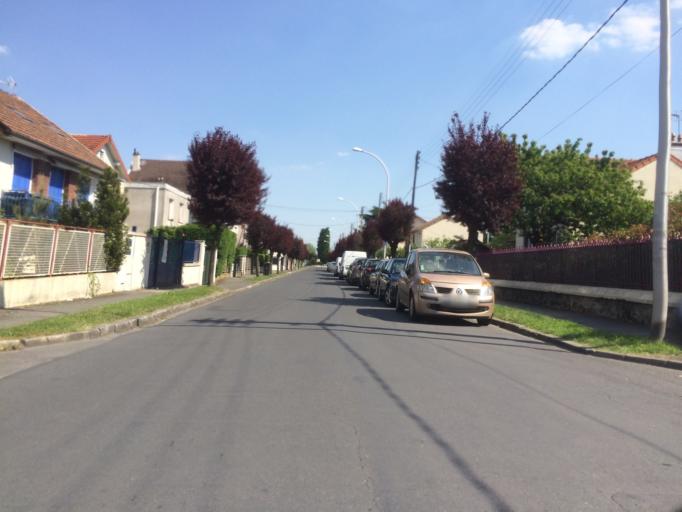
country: FR
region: Ile-de-France
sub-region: Departement de l'Essonne
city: Morangis
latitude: 48.6920
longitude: 2.3483
